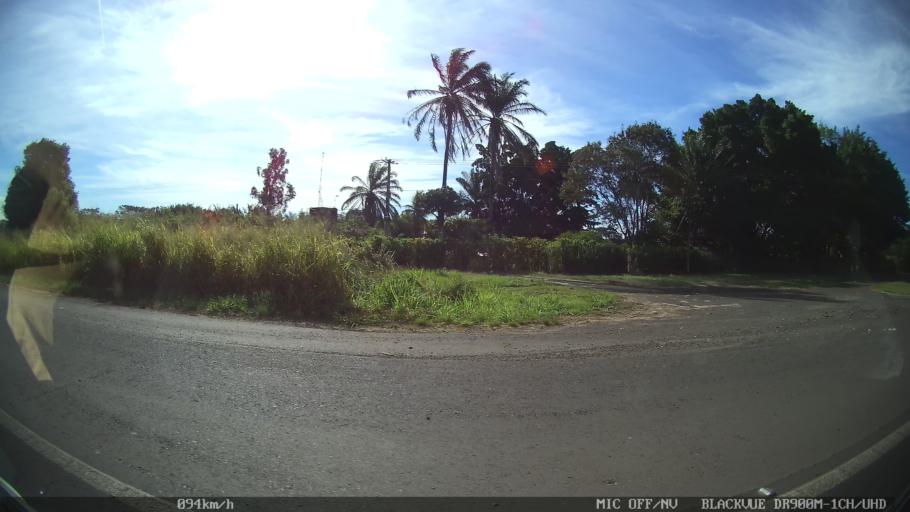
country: BR
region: Sao Paulo
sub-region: Sao Jose Do Rio Preto
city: Sao Jose do Rio Preto
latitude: -20.7953
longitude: -49.3165
